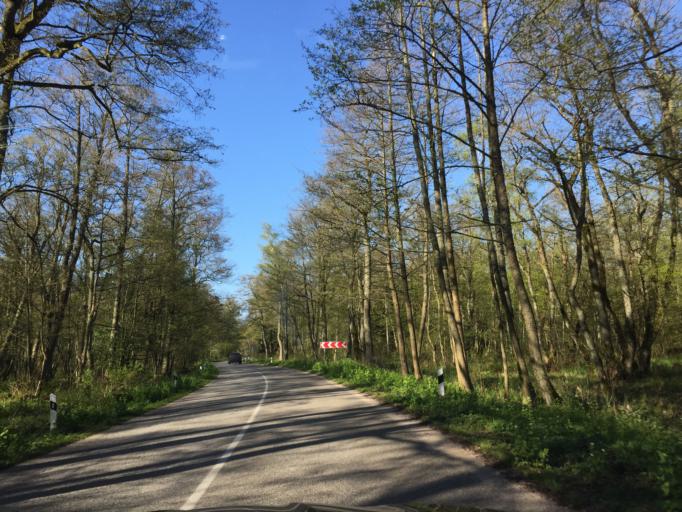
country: LT
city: Nida
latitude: 55.1869
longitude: 20.8569
